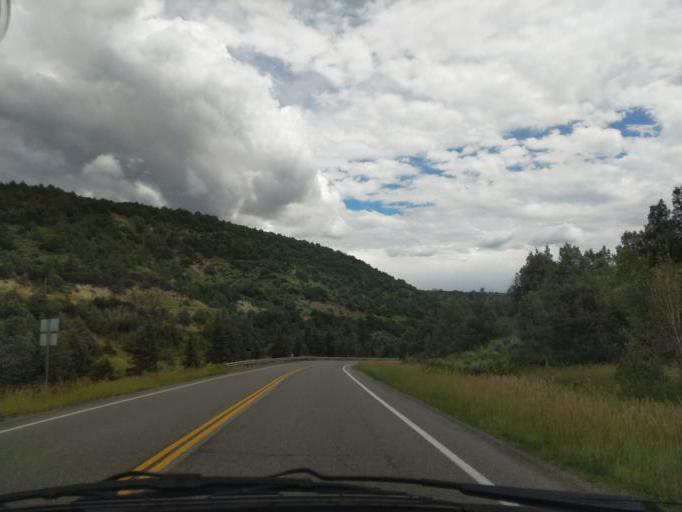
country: US
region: Colorado
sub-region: Delta County
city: Paonia
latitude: 39.0700
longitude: -107.3666
